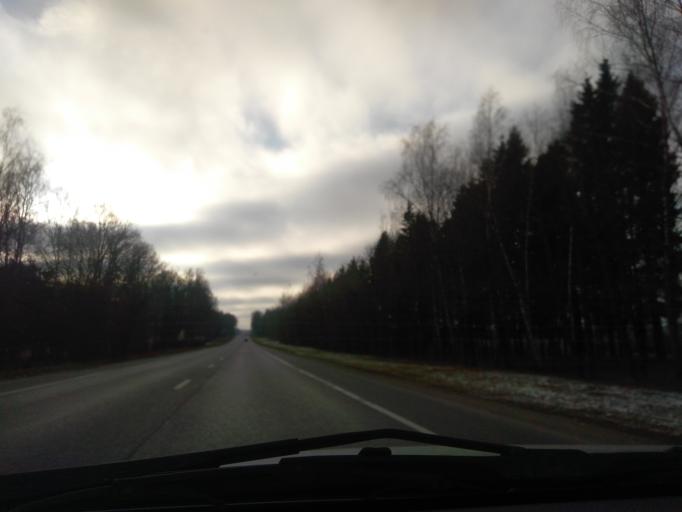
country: RU
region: Moskovskaya
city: Troitsk
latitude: 55.2972
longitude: 37.1349
